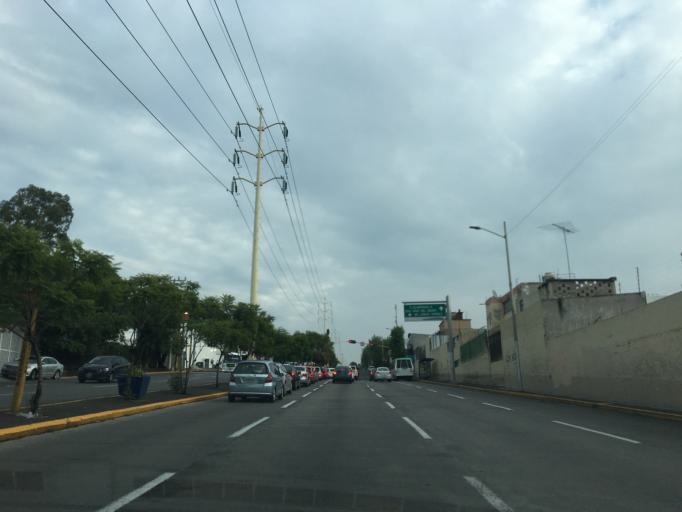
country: MX
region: Mexico
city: Naucalpan de Juarez
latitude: 19.5013
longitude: -99.2500
